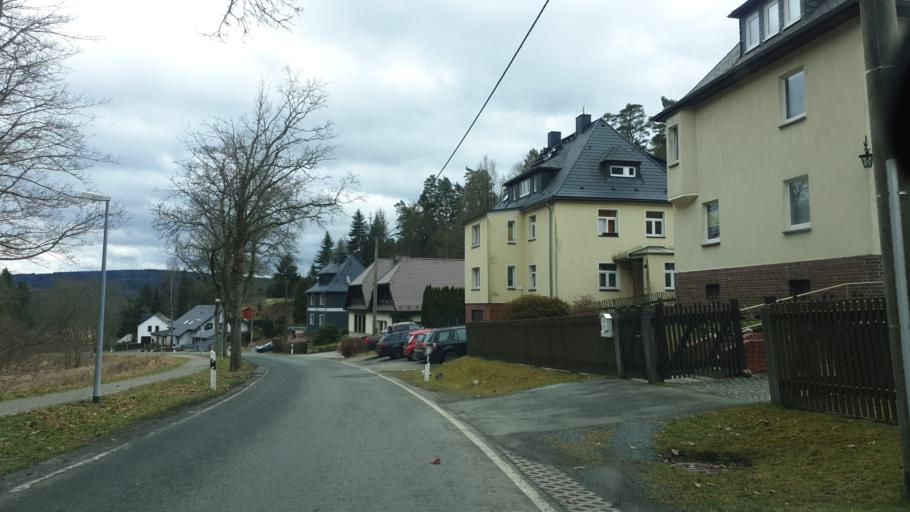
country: DE
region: Saxony
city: Bad Elster
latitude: 50.2887
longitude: 12.2249
